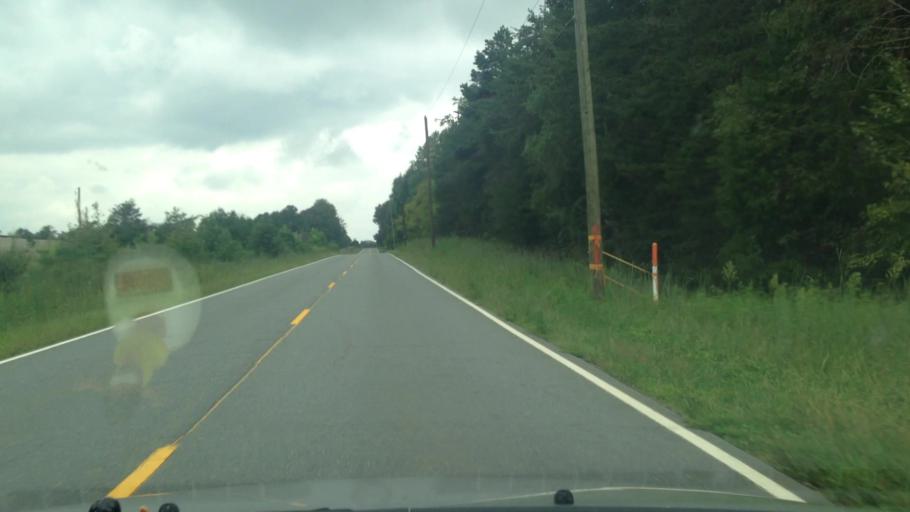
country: US
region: North Carolina
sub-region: Forsyth County
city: Walkertown
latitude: 36.2358
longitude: -80.1581
